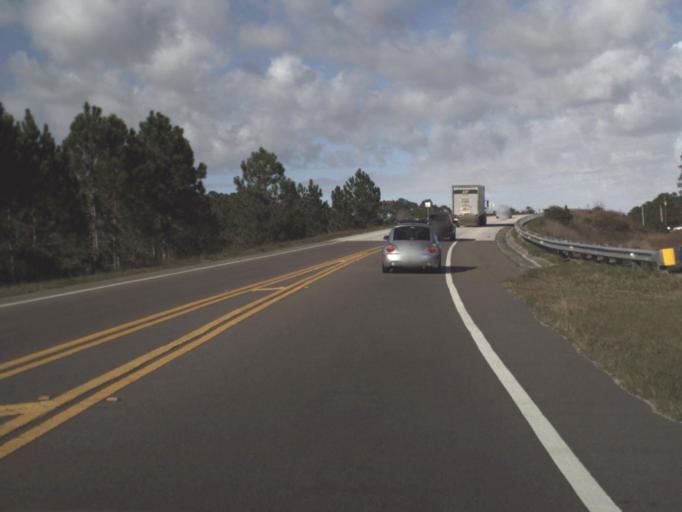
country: US
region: Florida
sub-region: Volusia County
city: Port Orange
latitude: 29.1193
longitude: -81.0484
